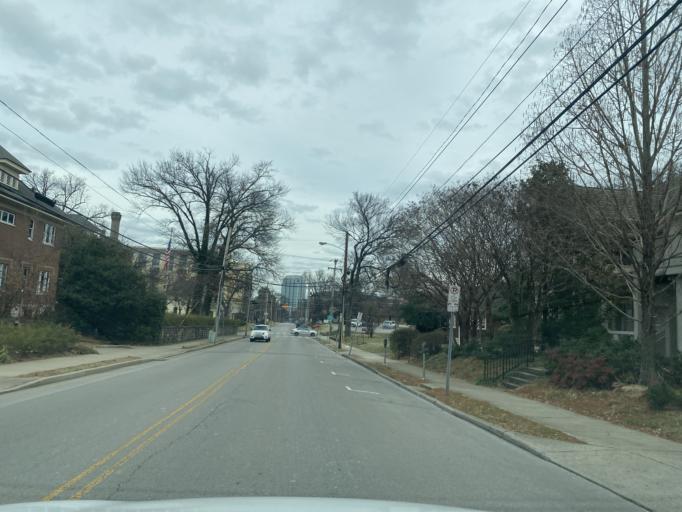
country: US
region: Tennessee
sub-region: Davidson County
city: Nashville
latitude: 36.1428
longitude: -86.7958
